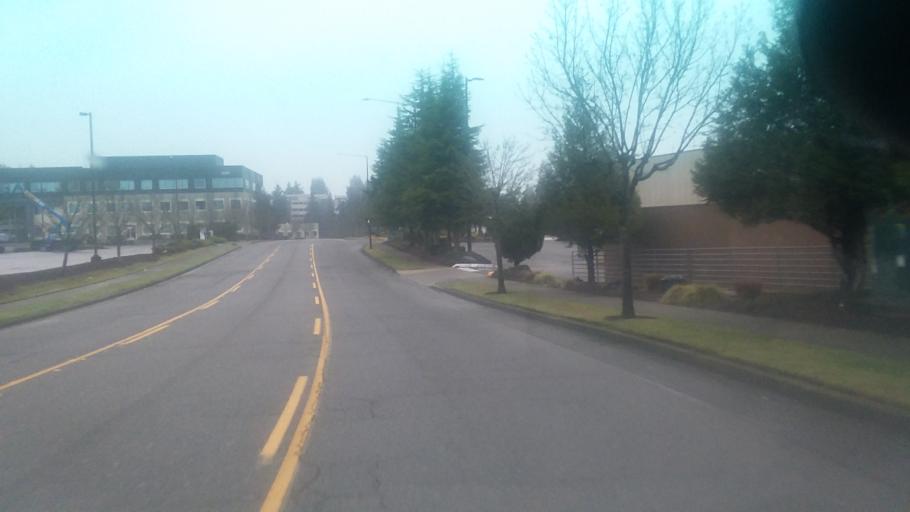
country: US
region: Washington
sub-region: Pierce County
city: Fircrest
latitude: 47.2384
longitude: -122.4801
